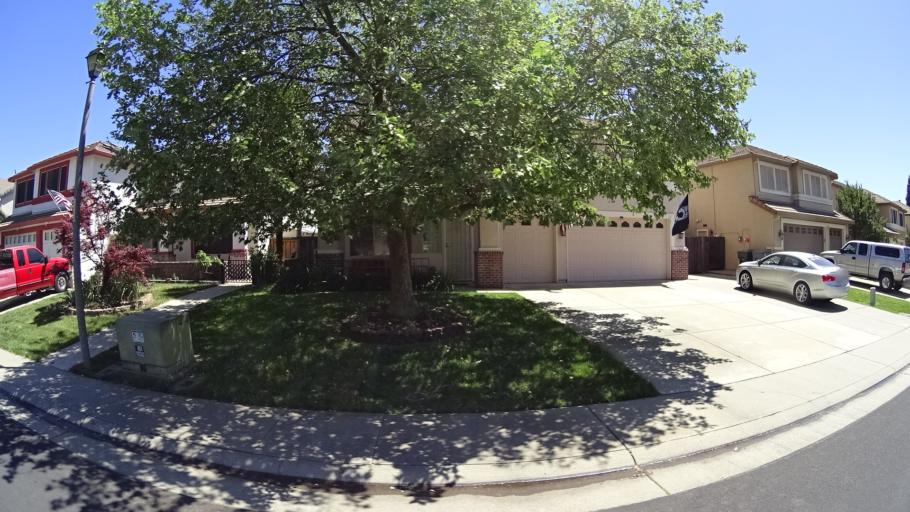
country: US
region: California
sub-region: Placer County
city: Rocklin
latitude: 38.8188
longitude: -121.2684
